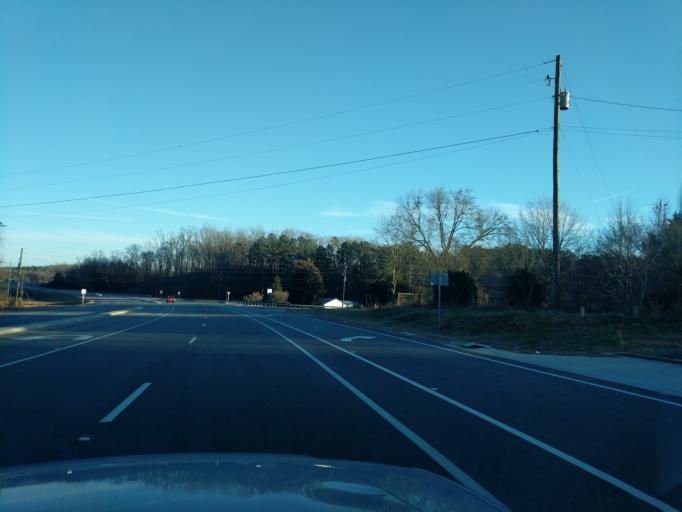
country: US
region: Georgia
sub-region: Stephens County
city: Toccoa
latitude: 34.5363
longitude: -83.2635
